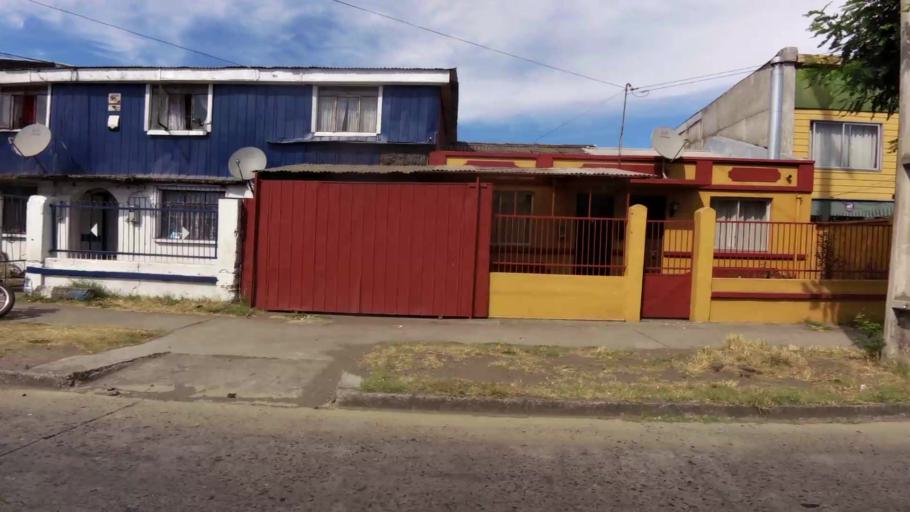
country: CL
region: Biobio
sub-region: Provincia de Concepcion
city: Talcahuano
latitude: -36.7227
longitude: -73.1225
